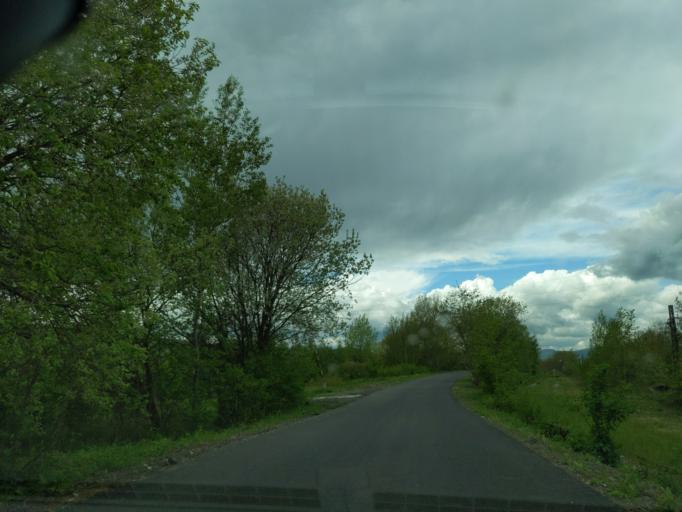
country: CZ
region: Ustecky
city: Trmice
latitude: 50.6461
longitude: 13.9792
